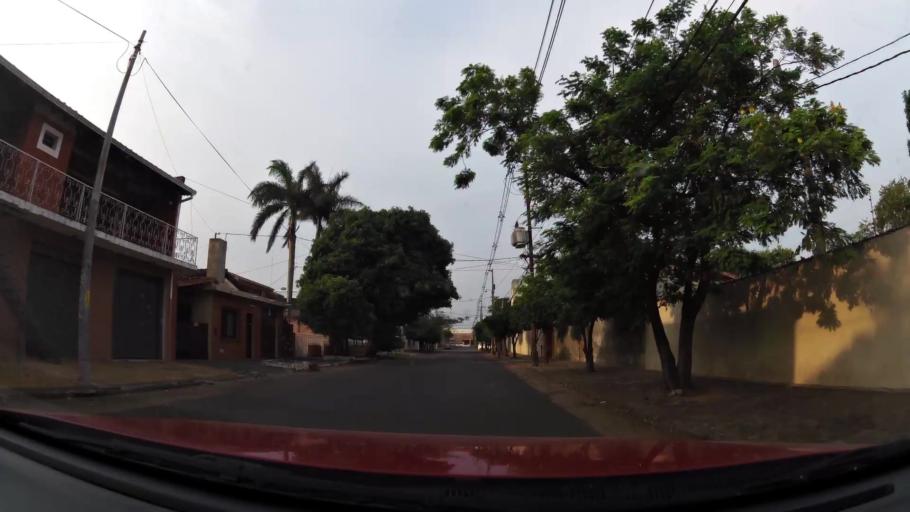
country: PY
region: Central
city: Lambare
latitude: -25.3204
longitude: -57.5691
